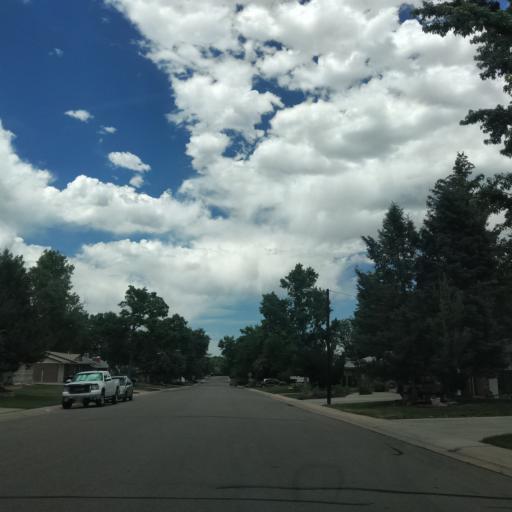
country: US
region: Colorado
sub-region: Jefferson County
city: Lakewood
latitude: 39.6868
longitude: -105.0909
